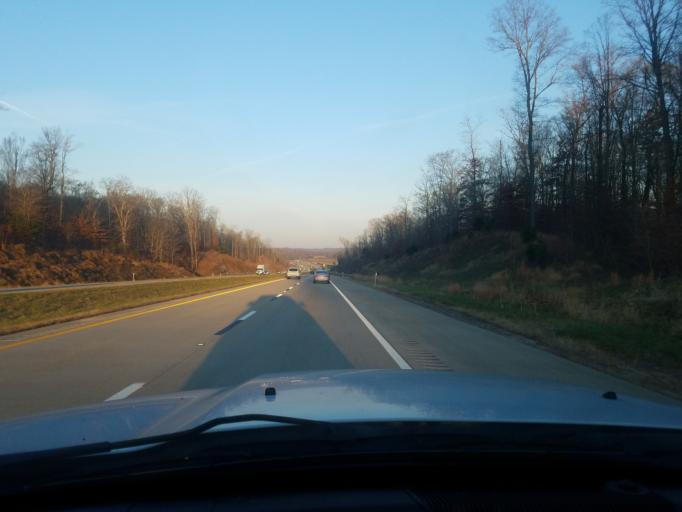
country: US
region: West Virginia
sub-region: Putnam County
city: Eleanor
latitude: 38.5416
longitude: -81.9665
